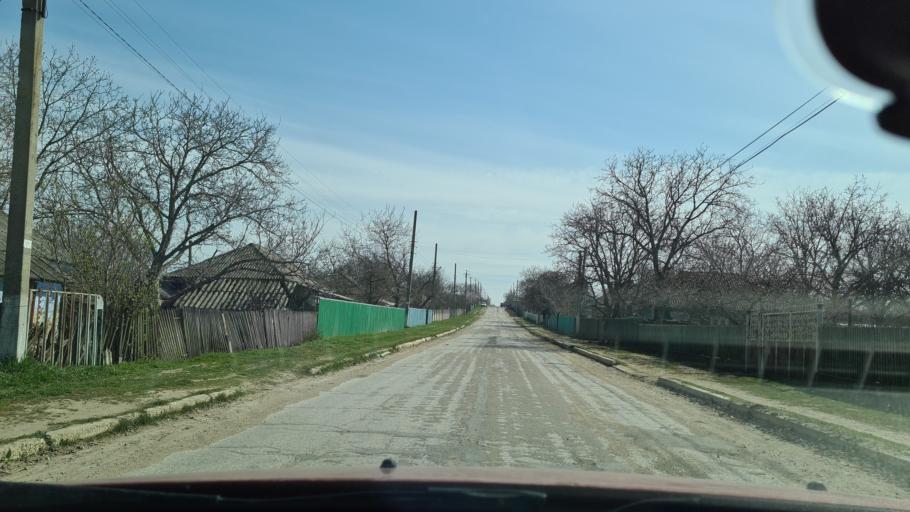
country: MD
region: Ungheni
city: Ungheni
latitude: 47.2690
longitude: 27.9388
